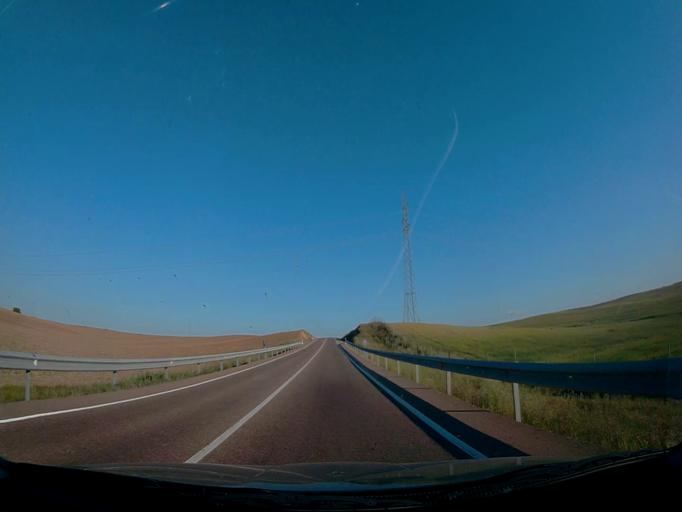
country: ES
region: Castille-La Mancha
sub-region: Province of Toledo
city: Hormigos
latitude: 40.1136
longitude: -4.4032
